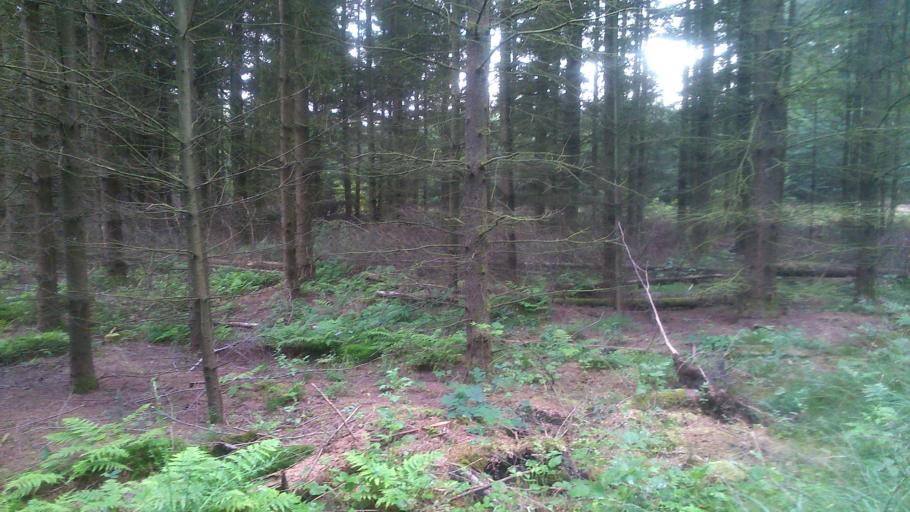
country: DK
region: Central Jutland
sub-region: Ringkobing-Skjern Kommune
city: Skjern
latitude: 56.0020
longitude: 8.4605
